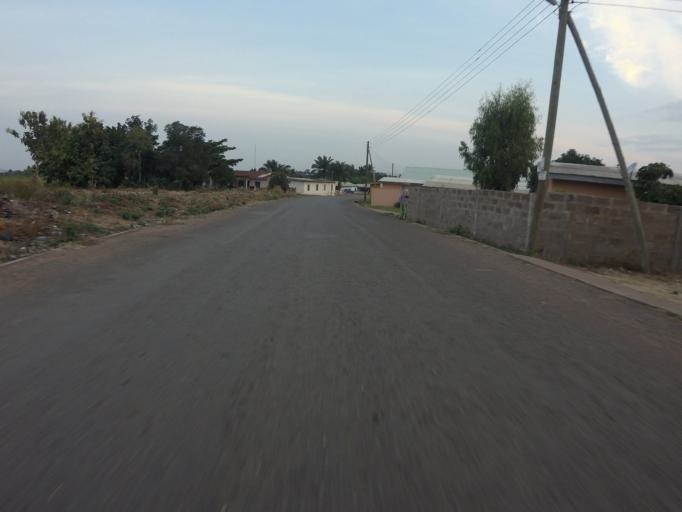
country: GH
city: Akropong
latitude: 6.1003
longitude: -0.0120
